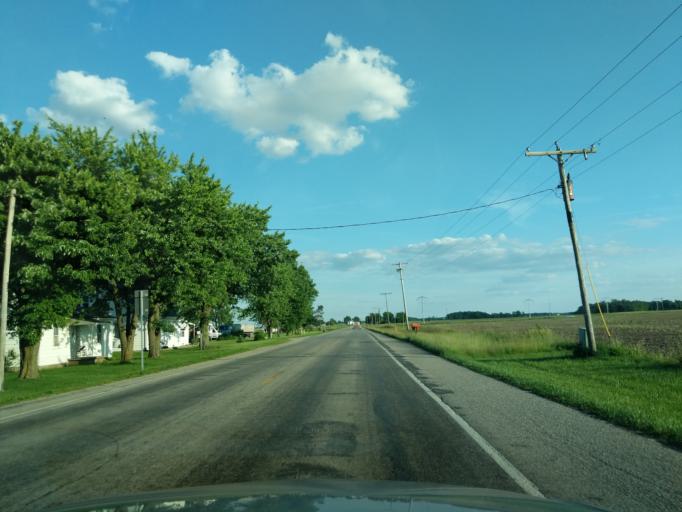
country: US
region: Indiana
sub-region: Huntington County
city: Warren
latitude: 40.7669
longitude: -85.4529
